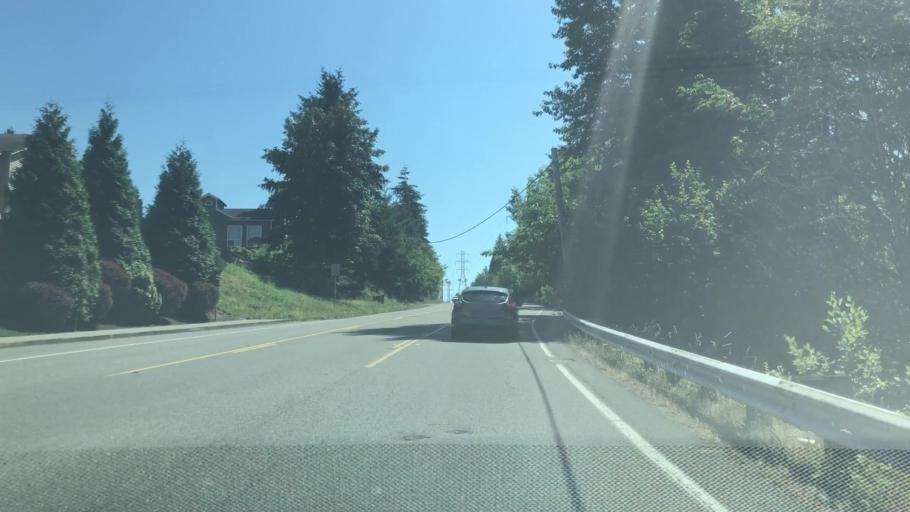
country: US
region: Washington
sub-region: King County
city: Woodinville
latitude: 47.7514
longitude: -122.1742
